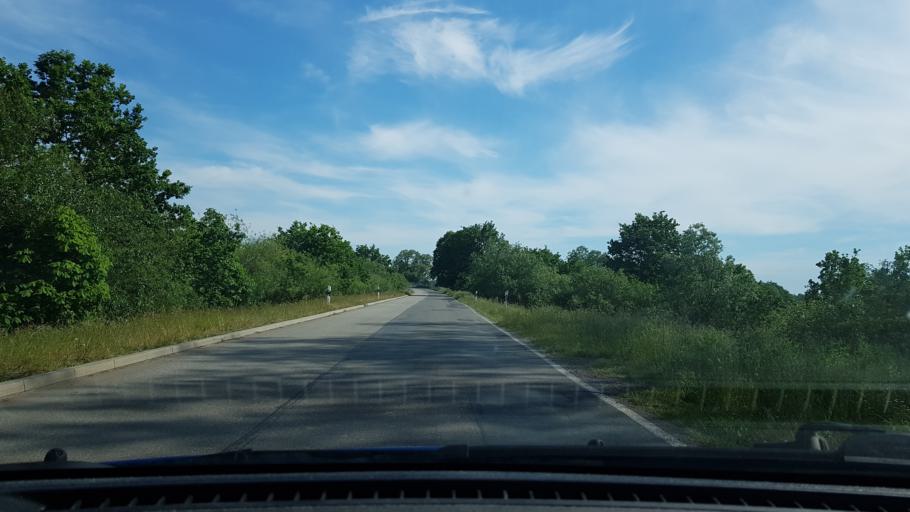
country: DE
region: Lower Saxony
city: Neu Darchau
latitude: 53.3401
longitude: 10.8599
